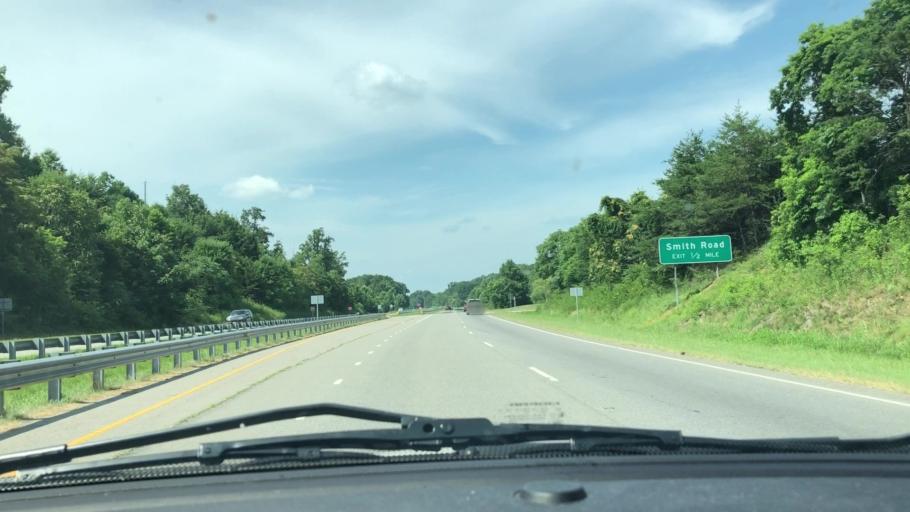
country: US
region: North Carolina
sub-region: Rockingham County
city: Stoneville
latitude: 36.4913
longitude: -79.9249
